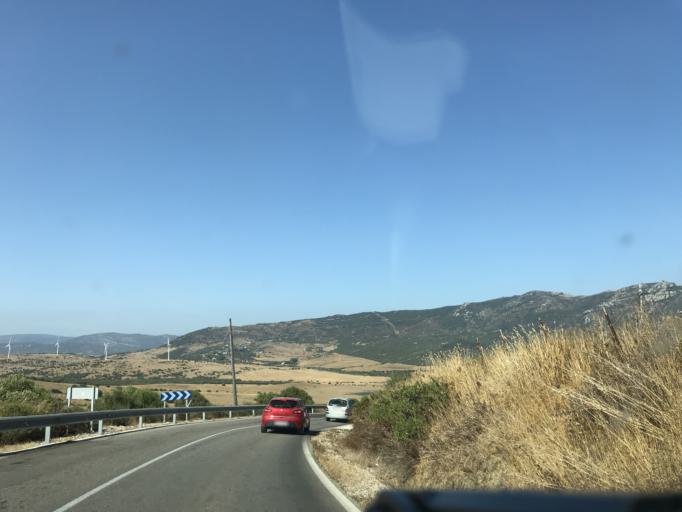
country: ES
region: Andalusia
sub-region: Provincia de Cadiz
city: Zahara de los Atunes
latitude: 36.1013
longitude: -5.7296
